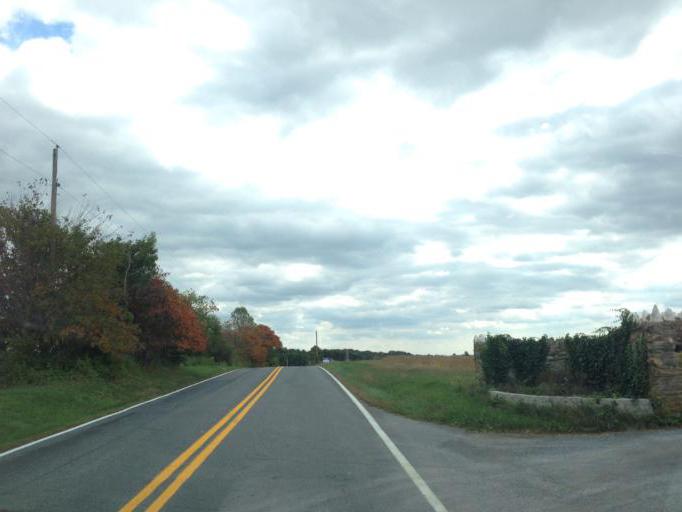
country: US
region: Maryland
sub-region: Carroll County
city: Mount Airy
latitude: 39.2813
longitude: -77.0868
